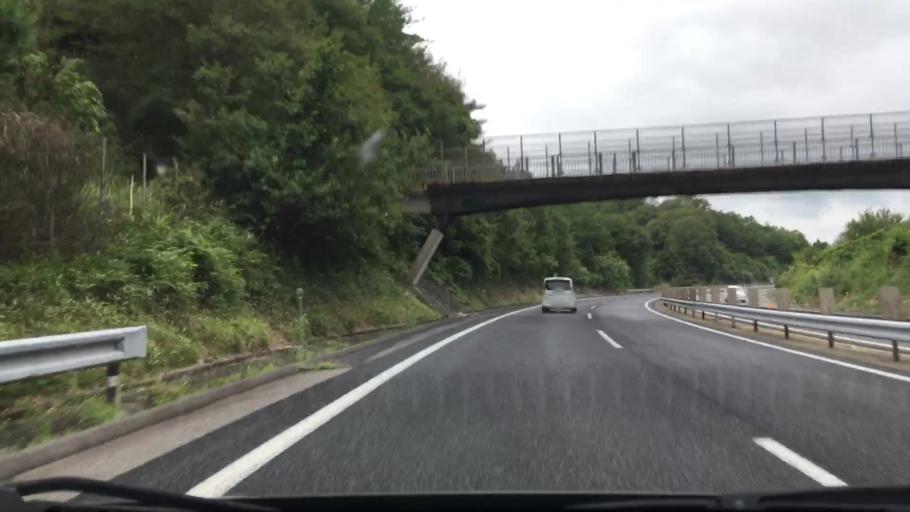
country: JP
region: Hiroshima
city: Miyoshi
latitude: 34.7439
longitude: 132.7220
